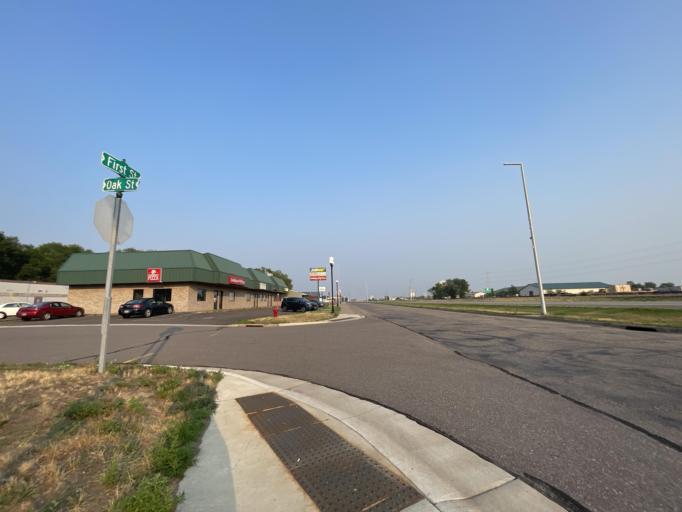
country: US
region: Minnesota
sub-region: Sherburne County
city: Becker
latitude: 45.3913
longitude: -93.8740
